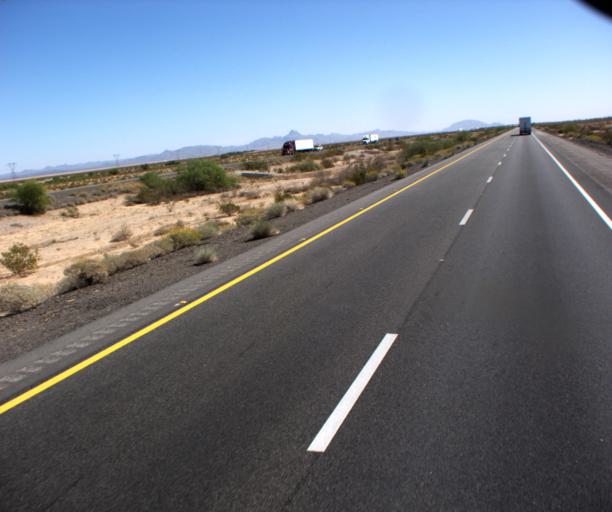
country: US
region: Arizona
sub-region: La Paz County
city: Salome
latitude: 33.5736
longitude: -113.3854
